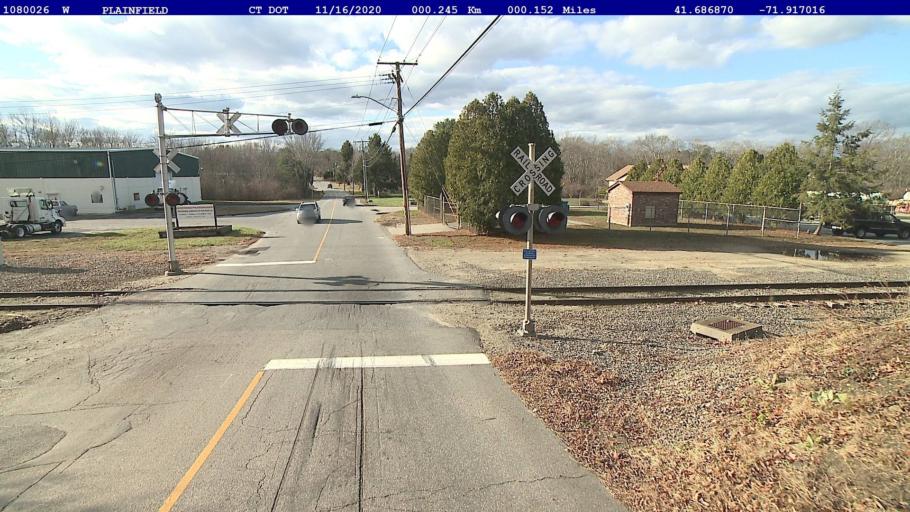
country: US
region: Connecticut
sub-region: Windham County
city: Plainfield
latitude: 41.6869
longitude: -71.9170
